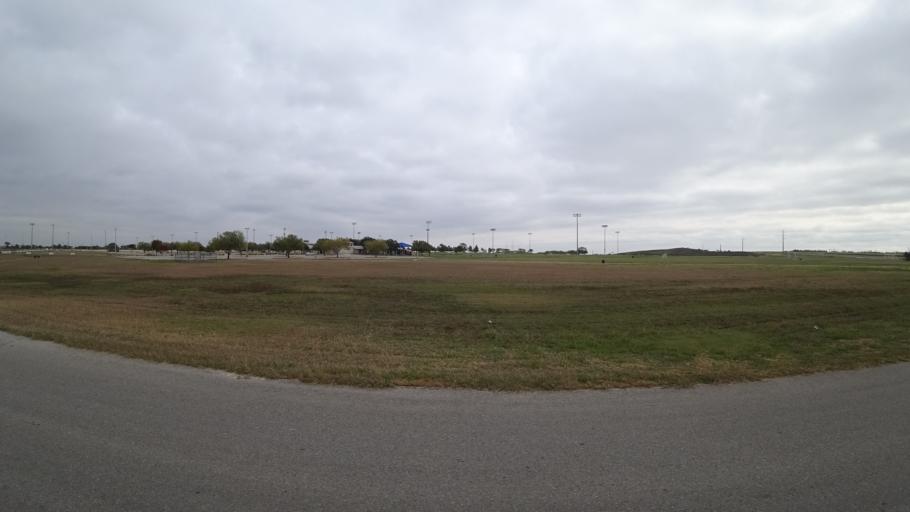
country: US
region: Texas
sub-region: Travis County
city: Pflugerville
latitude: 30.4107
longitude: -97.5994
